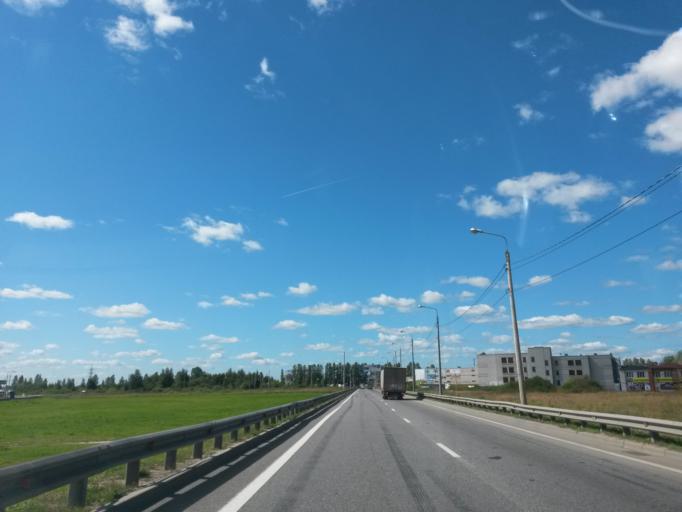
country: RU
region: Jaroslavl
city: Yaroslavl
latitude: 57.6705
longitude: 39.7795
